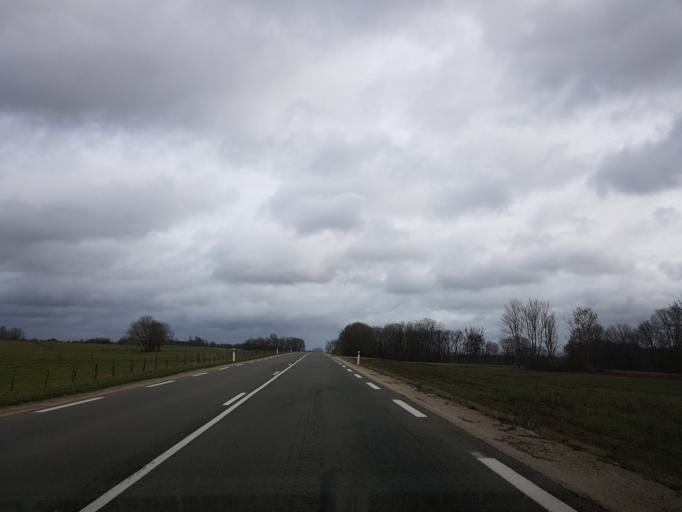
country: FR
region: Champagne-Ardenne
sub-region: Departement de la Haute-Marne
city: Chalindrey
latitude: 47.8437
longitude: 5.4558
